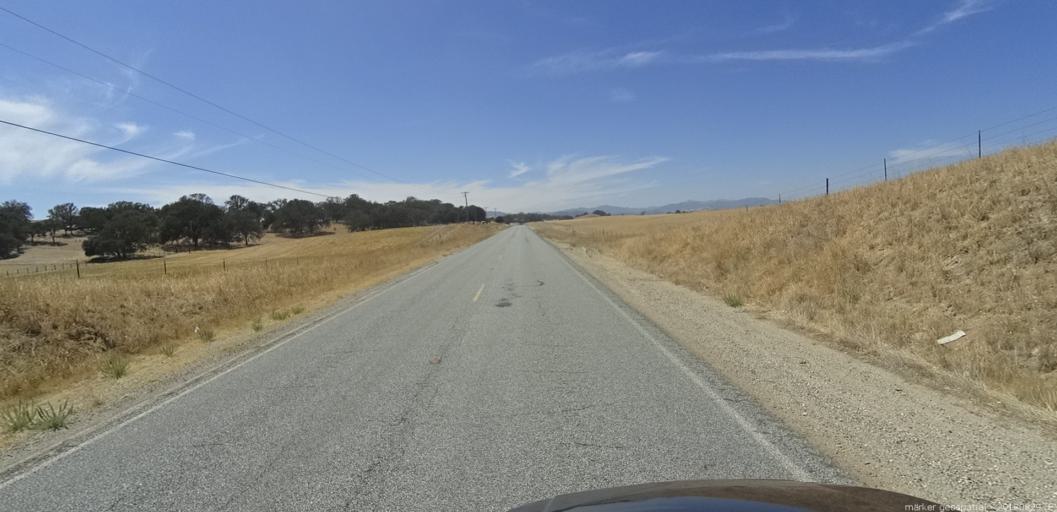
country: US
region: California
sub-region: Monterey County
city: King City
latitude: 35.9370
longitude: -121.0936
